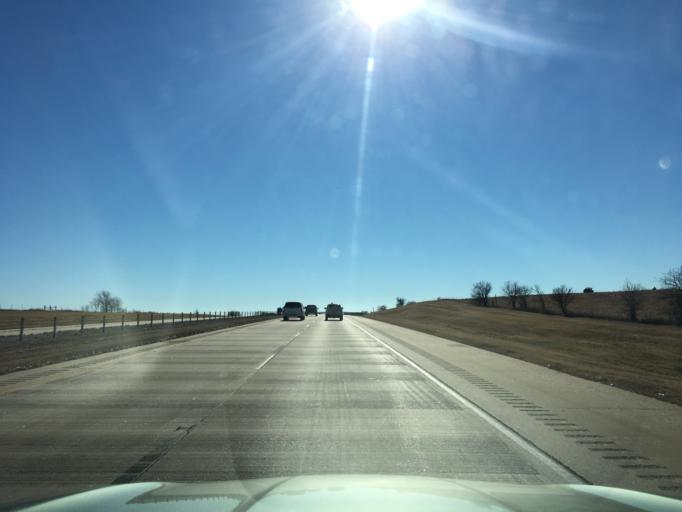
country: US
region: Oklahoma
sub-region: Noble County
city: Perry
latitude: 36.4547
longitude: -97.3271
